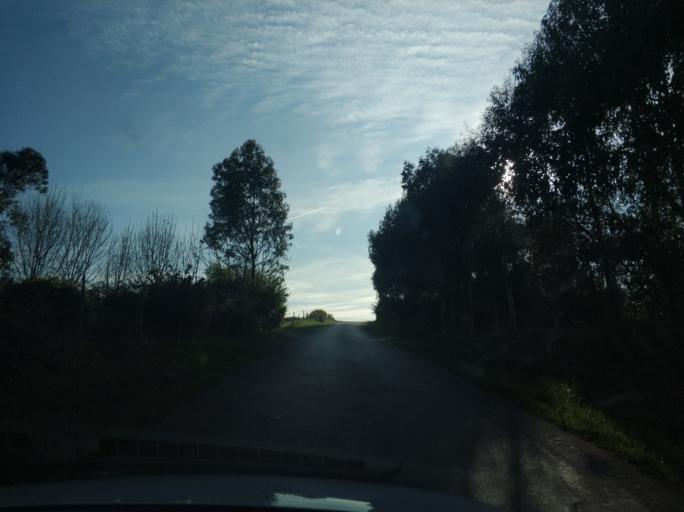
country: ES
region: Cantabria
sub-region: Provincia de Cantabria
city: Comillas
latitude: 43.3896
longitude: -4.3059
